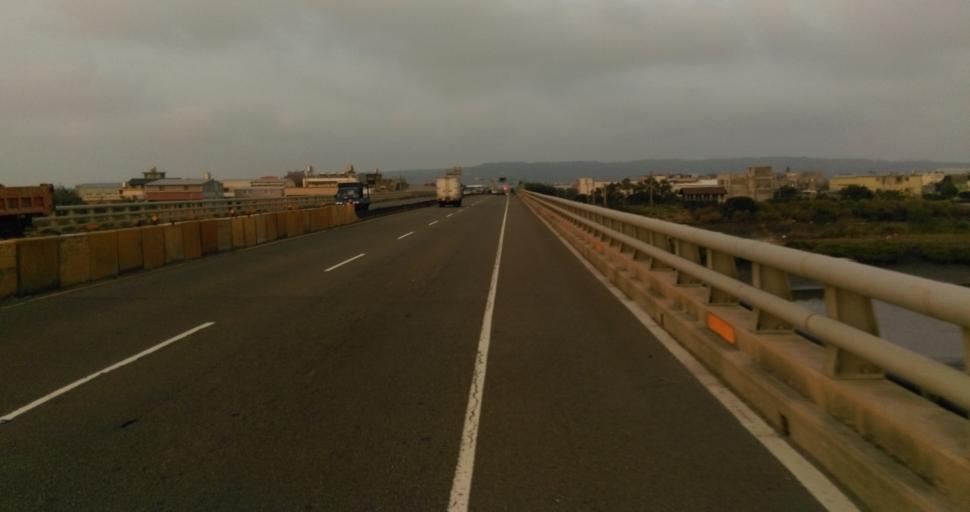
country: TW
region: Taiwan
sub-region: Hsinchu
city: Hsinchu
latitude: 24.8492
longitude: 120.9403
